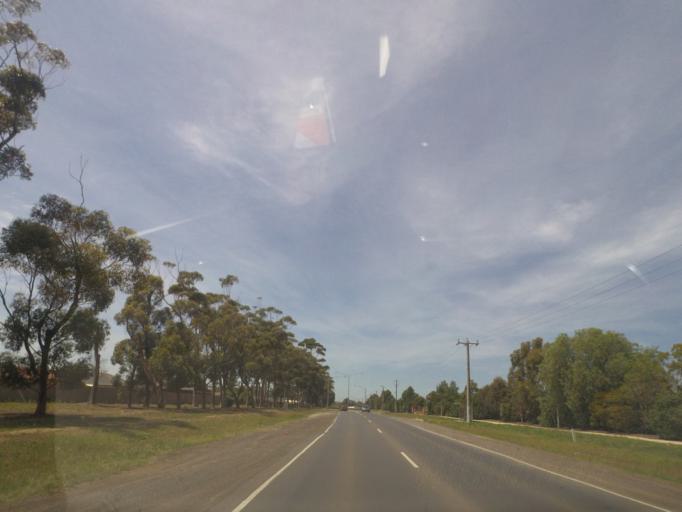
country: AU
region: Victoria
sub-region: Wyndham
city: Tarneit
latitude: -37.8827
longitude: 144.6225
